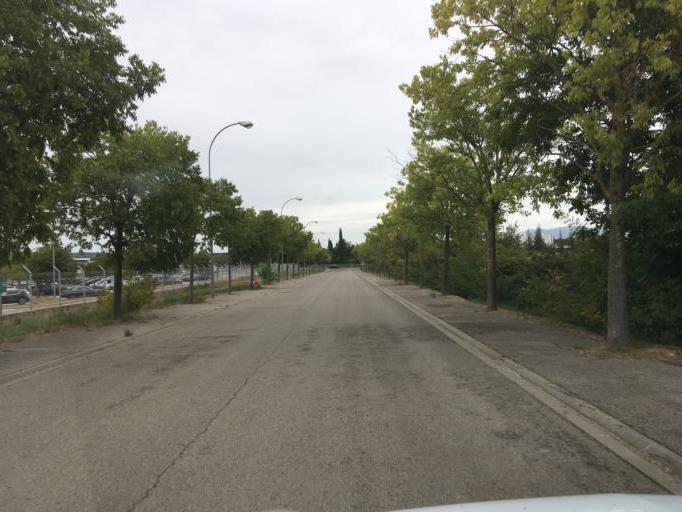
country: FR
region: Provence-Alpes-Cote d'Azur
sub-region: Departement des Bouches-du-Rhone
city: Rousset
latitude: 43.4713
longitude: 5.6038
